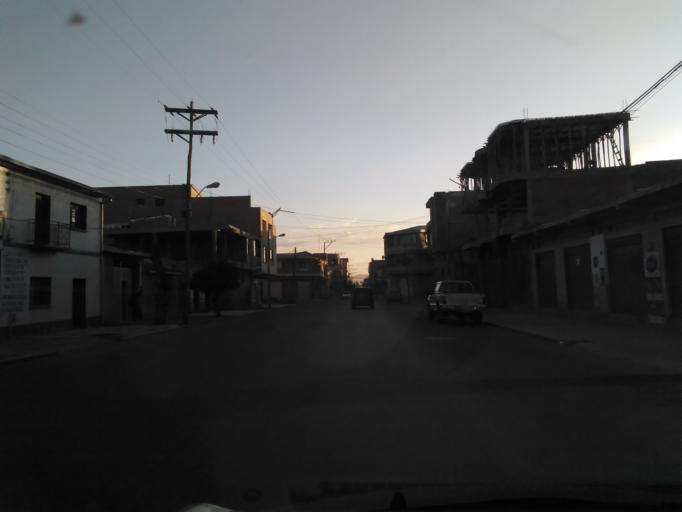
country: BO
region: Cochabamba
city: Punata
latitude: -17.5482
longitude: -65.8346
